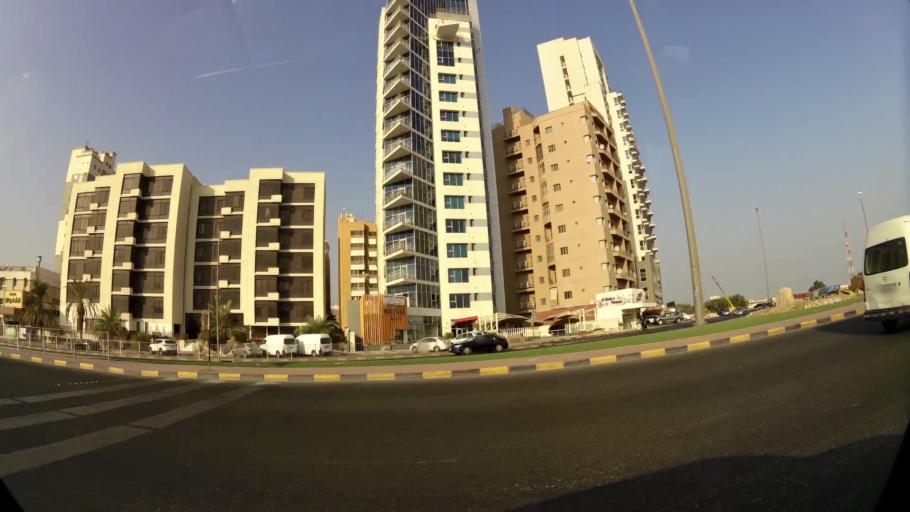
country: KW
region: Muhafazat Hawalli
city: As Salimiyah
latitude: 29.3235
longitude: 48.0874
